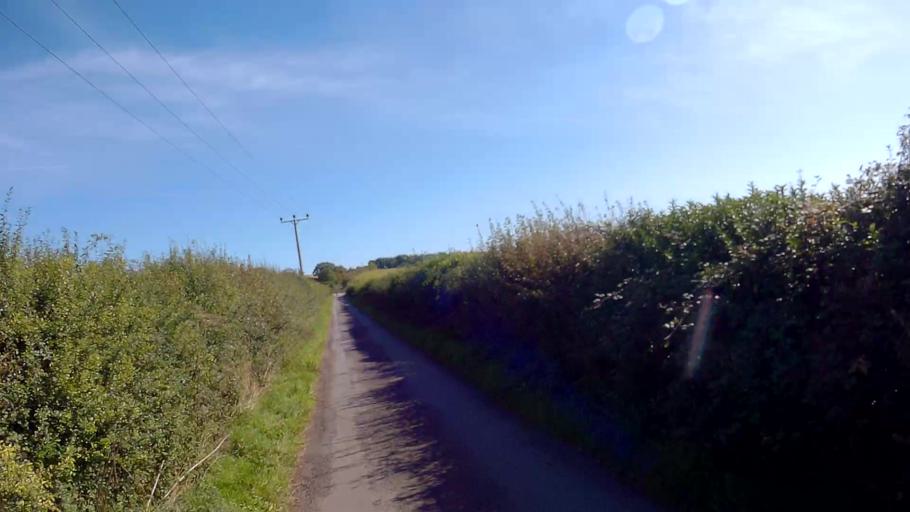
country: GB
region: England
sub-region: Hampshire
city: Andover
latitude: 51.1626
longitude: -1.4051
